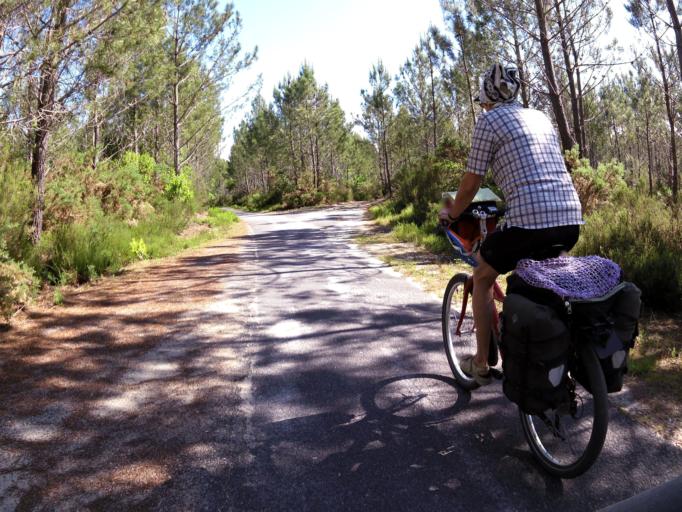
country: FR
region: Aquitaine
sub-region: Departement de la Gironde
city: Lacanau
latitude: 45.0336
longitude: -1.1565
